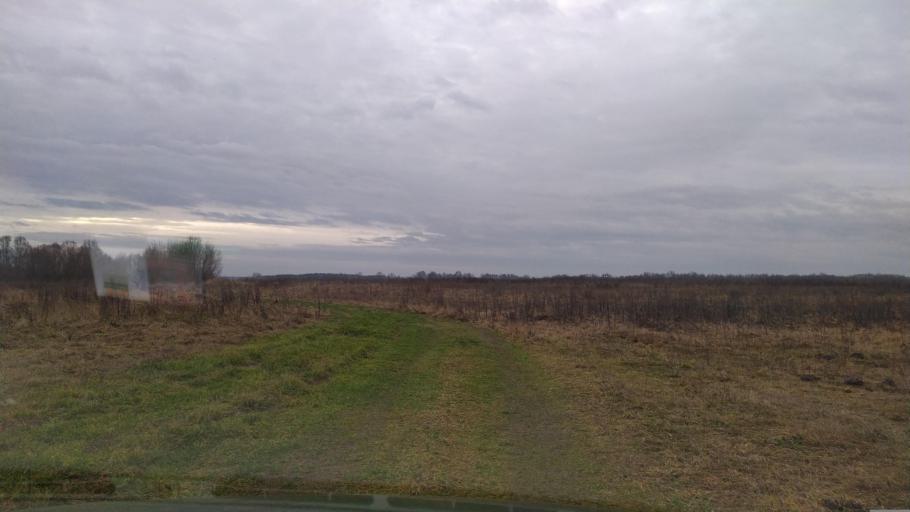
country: BY
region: Brest
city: Kamyanyets
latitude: 52.4365
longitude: 23.8475
